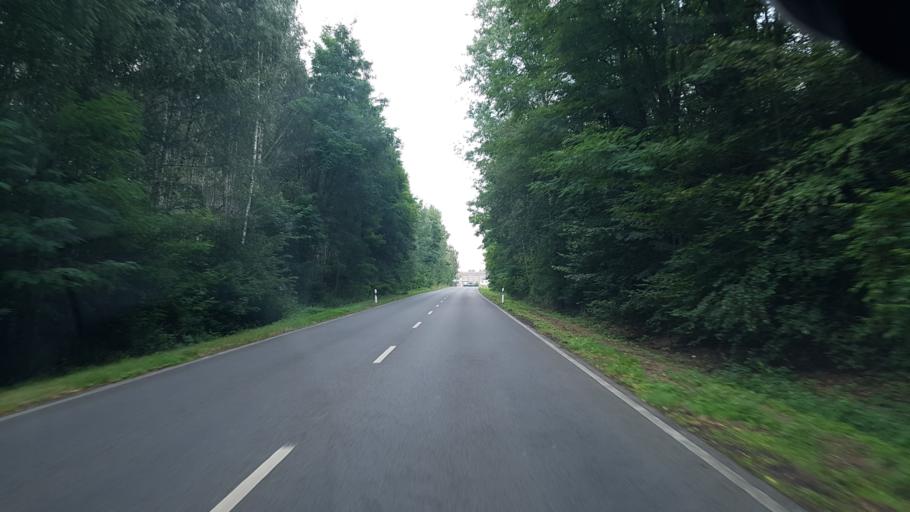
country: DE
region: Brandenburg
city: Lauchhammer
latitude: 51.4940
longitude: 13.7403
